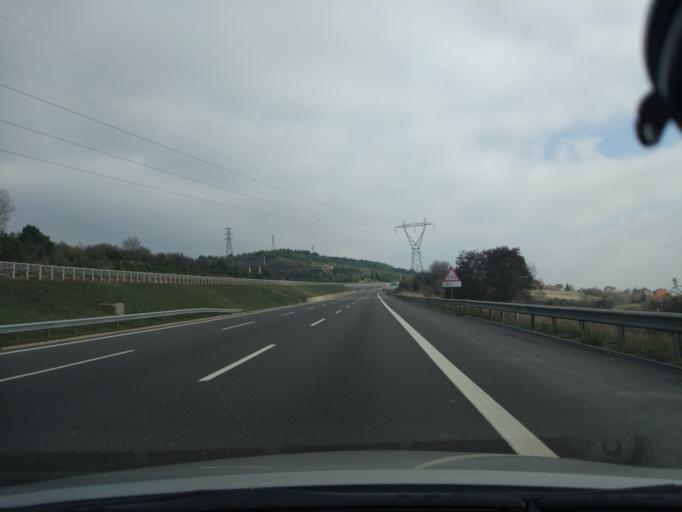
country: TR
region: Bolu
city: Bolu
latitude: 40.7302
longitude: 31.5157
